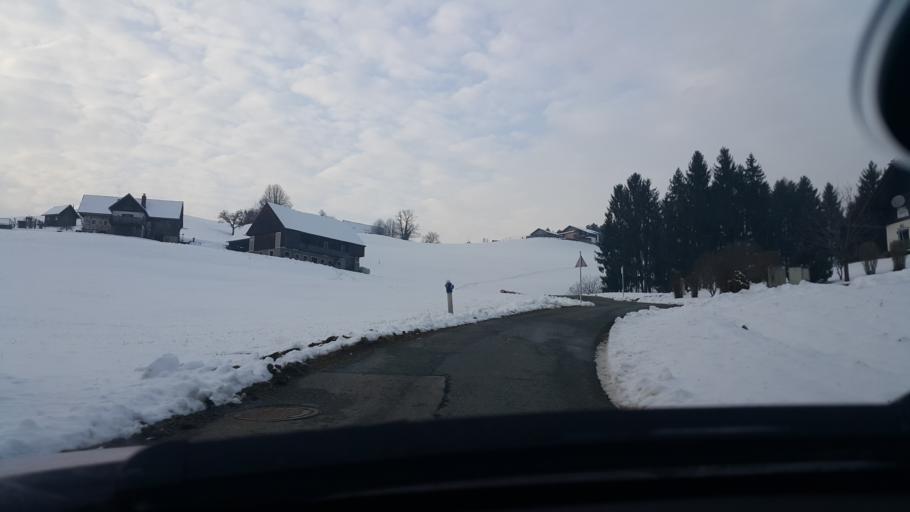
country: AT
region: Styria
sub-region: Politischer Bezirk Graz-Umgebung
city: Sankt Oswald bei Plankenwarth
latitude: 47.0886
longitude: 15.2498
